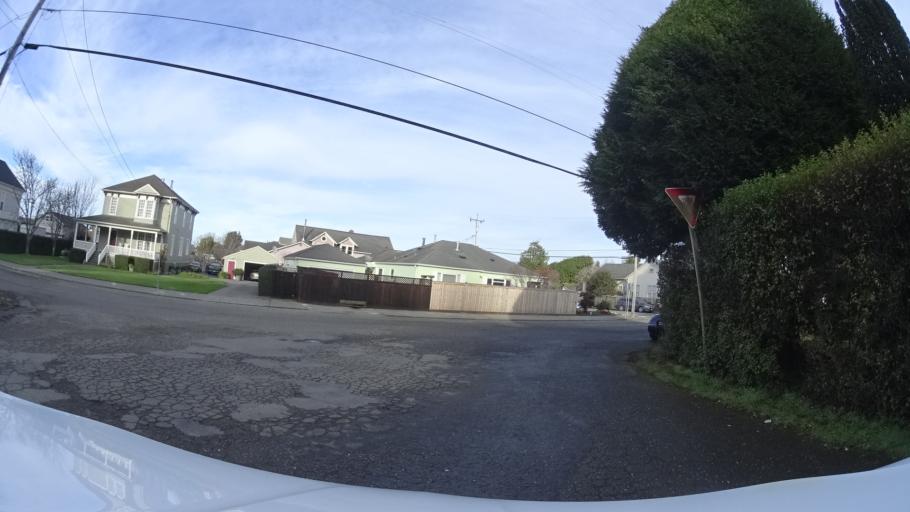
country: US
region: California
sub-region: Humboldt County
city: Ferndale
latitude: 40.5762
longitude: -124.2666
